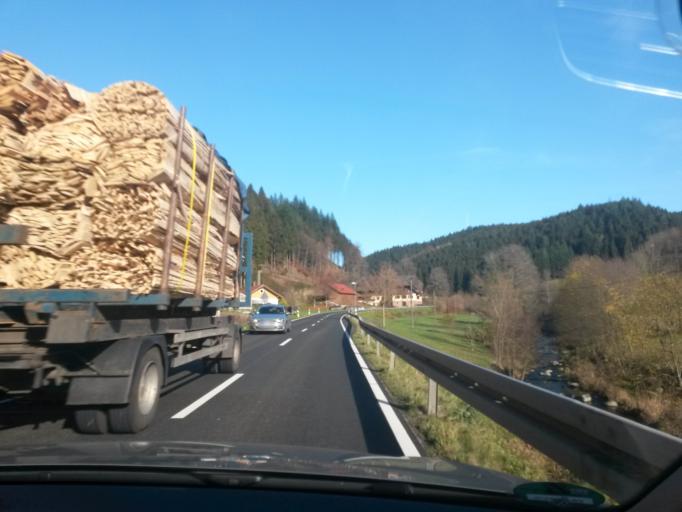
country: DE
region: Baden-Wuerttemberg
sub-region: Karlsruhe Region
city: Bad Rippoldsau-Schapbach
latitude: 48.3657
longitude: 8.2771
